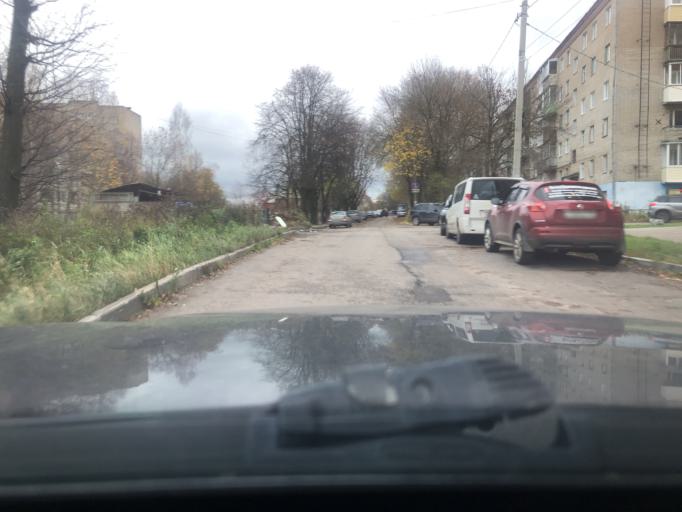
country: RU
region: Moskovskaya
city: Sergiyev Posad
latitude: 56.2971
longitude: 38.1164
